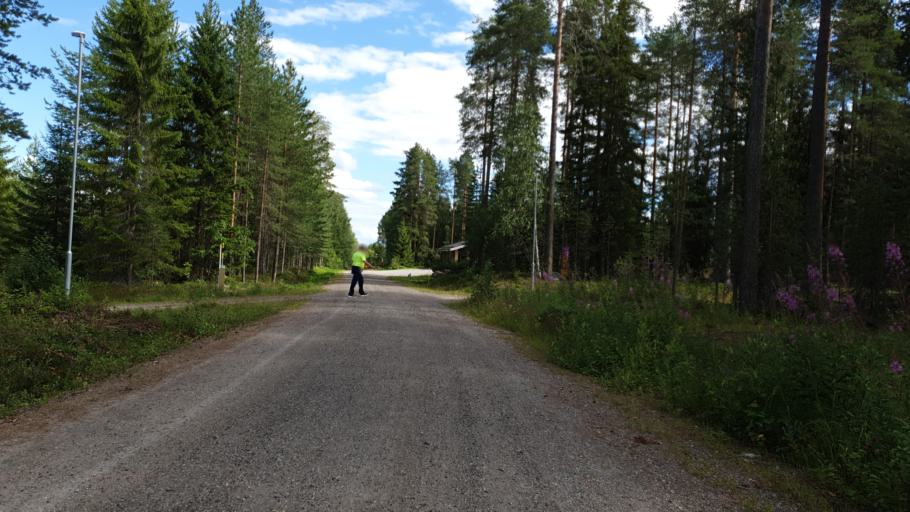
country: FI
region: Kainuu
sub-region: Kehys-Kainuu
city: Kuhmo
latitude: 64.1149
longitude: 29.5167
